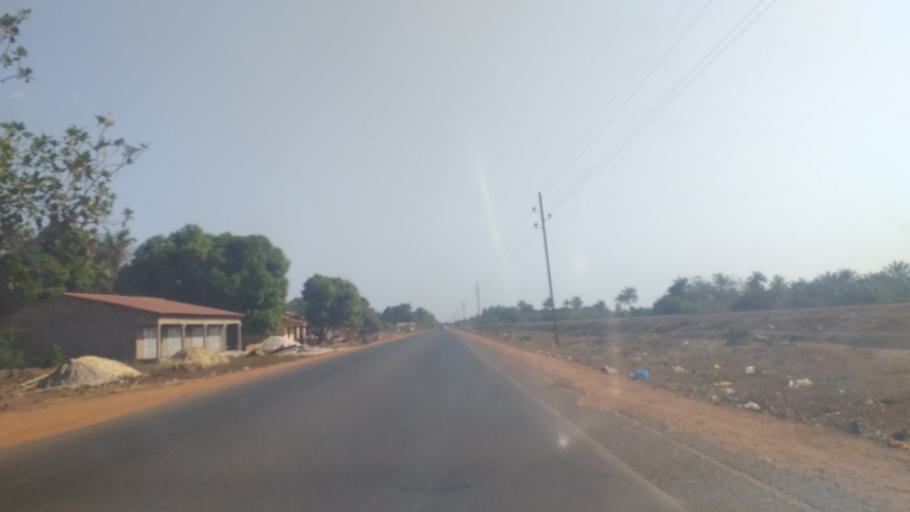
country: GN
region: Boke
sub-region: Boke Prefecture
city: Kamsar
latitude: 10.7192
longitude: -14.5210
